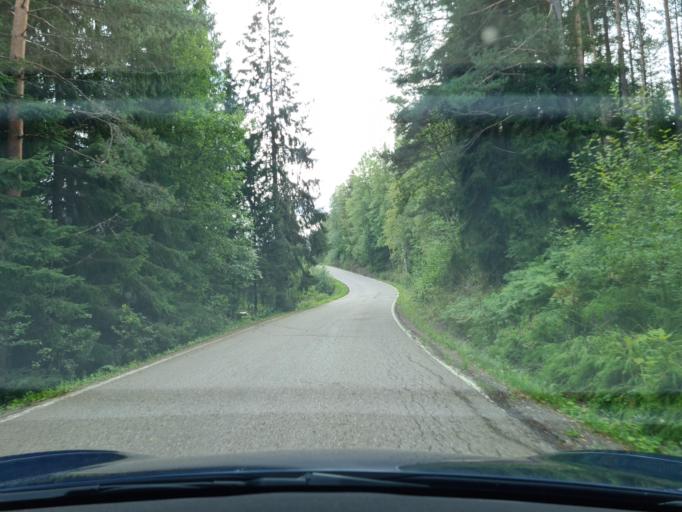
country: FI
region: Uusimaa
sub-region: Helsinki
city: Vihti
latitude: 60.4678
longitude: 24.4420
